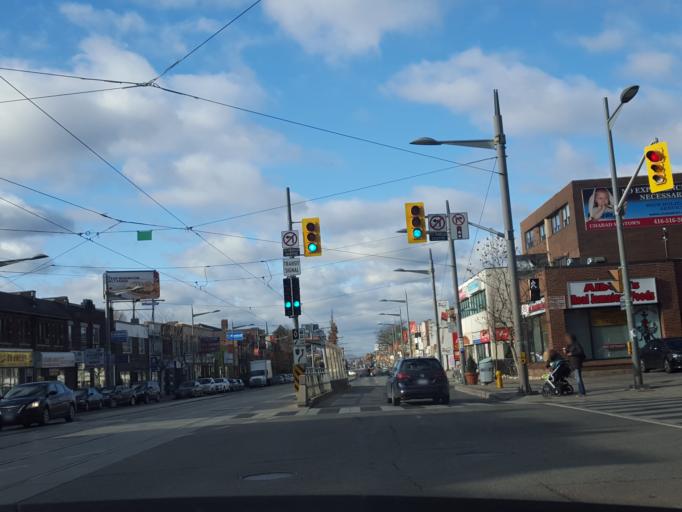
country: CA
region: Ontario
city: Toronto
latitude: 43.6829
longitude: -79.4201
